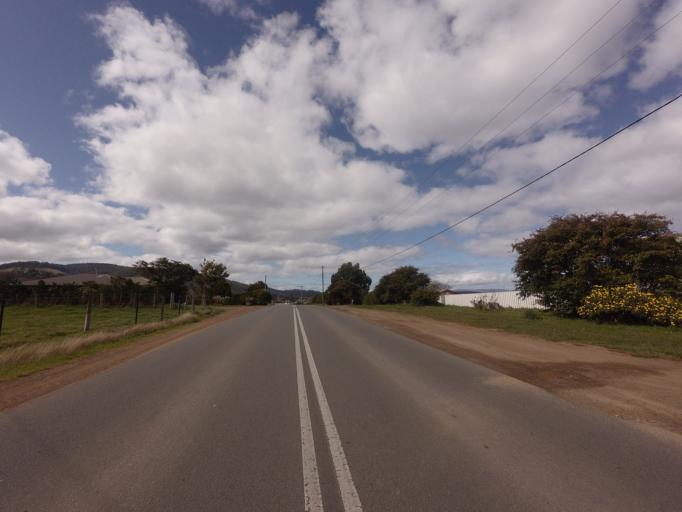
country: AU
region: Tasmania
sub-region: Huon Valley
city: Geeveston
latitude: -43.3214
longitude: 147.0050
